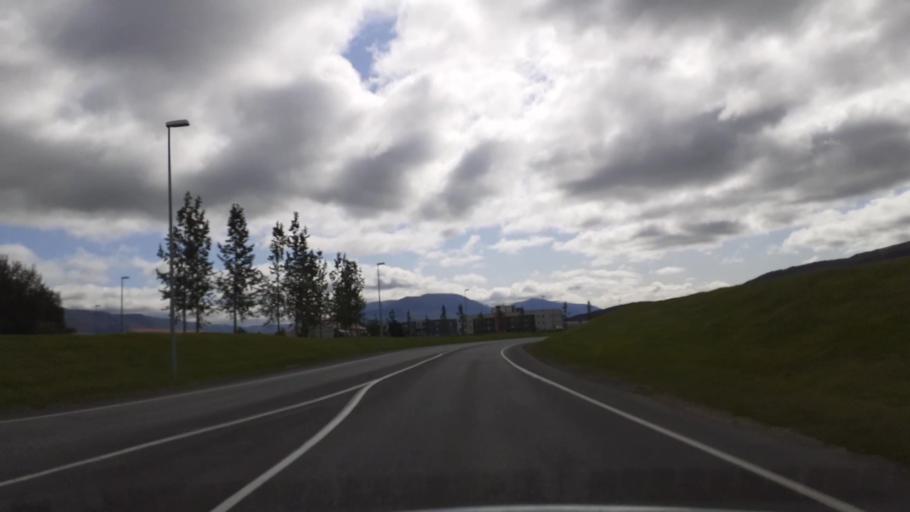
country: IS
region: Northeast
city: Akureyri
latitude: 65.6715
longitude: -18.1078
